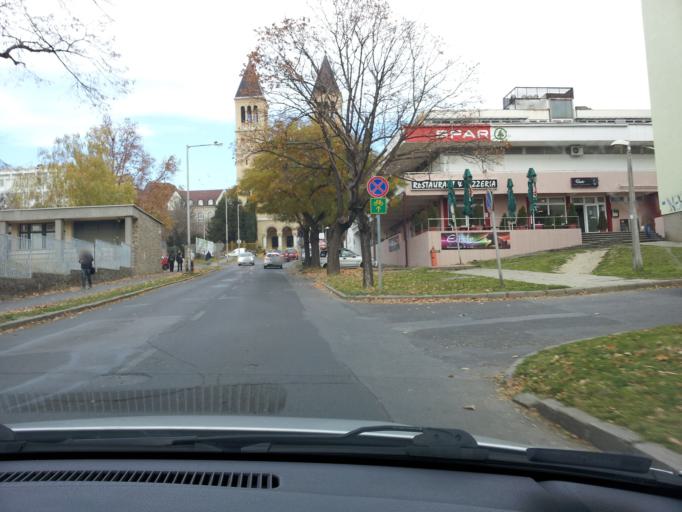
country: HU
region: Baranya
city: Pecs
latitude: 46.0750
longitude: 18.2077
